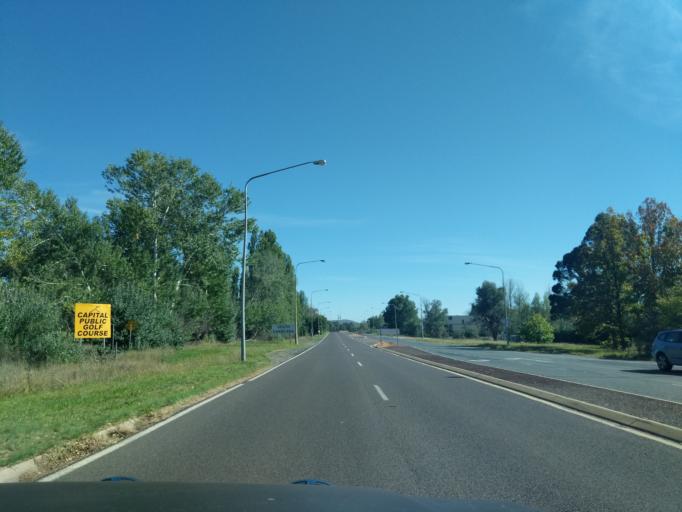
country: AU
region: Australian Capital Territory
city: Forrest
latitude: -35.3427
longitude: 149.1539
